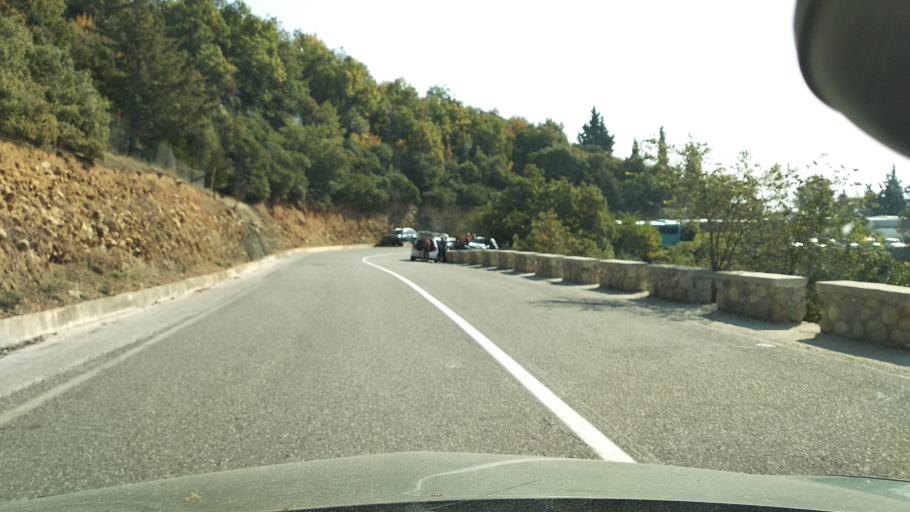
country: GR
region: Thessaly
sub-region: Trikala
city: Kalampaka
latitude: 39.7105
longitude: 21.6389
